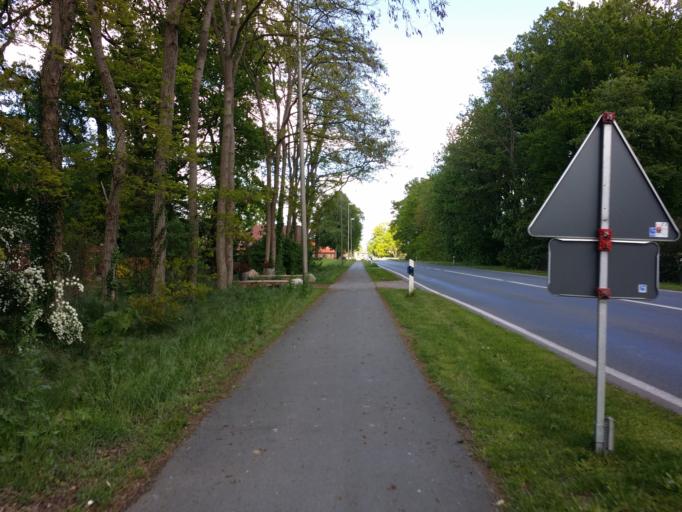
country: DE
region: Lower Saxony
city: Delmenhorst
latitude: 53.0179
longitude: 8.6076
